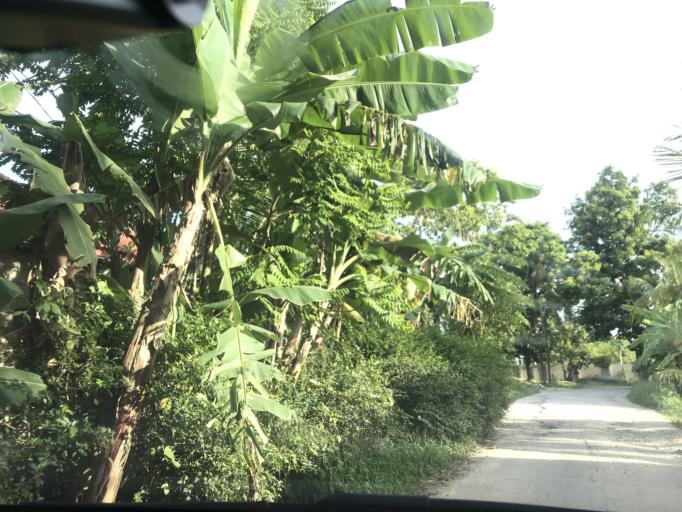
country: MY
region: Kelantan
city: Kota Bharu
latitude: 6.1306
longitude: 102.2217
